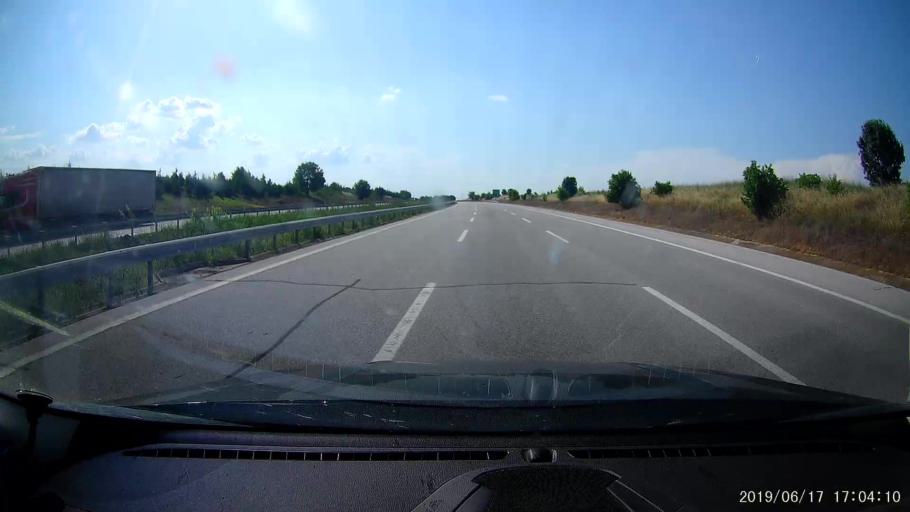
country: TR
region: Edirne
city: Haskoy
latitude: 41.6521
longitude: 26.7345
